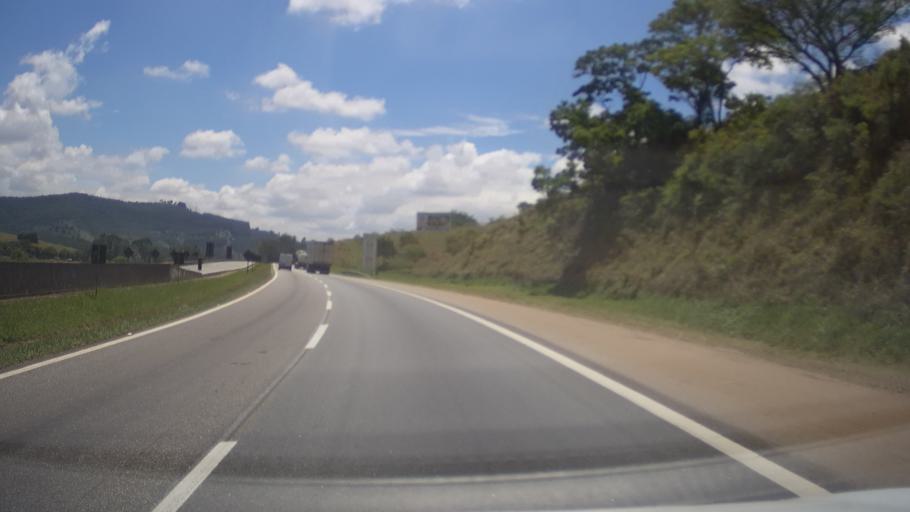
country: BR
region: Minas Gerais
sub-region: Campanha
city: Campanha
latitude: -21.8307
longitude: -45.4981
